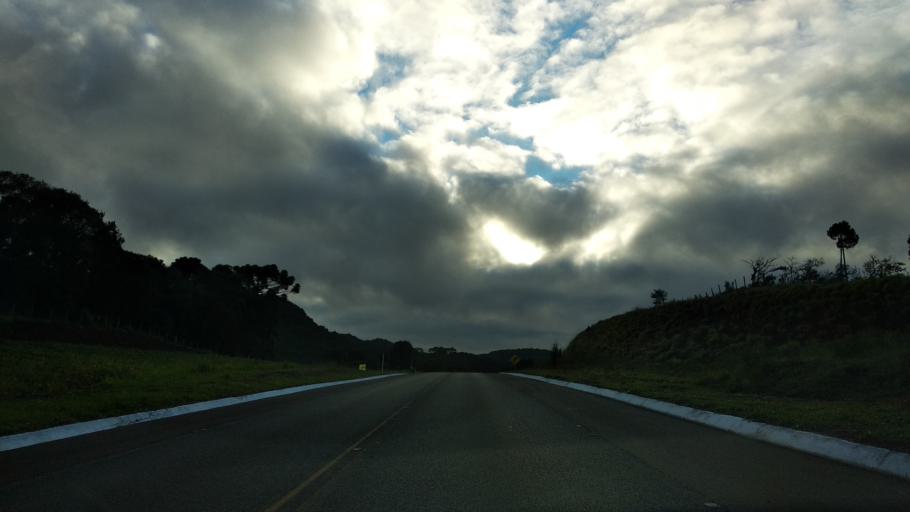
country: BR
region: Santa Catarina
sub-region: Curitibanos
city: Curitibanos
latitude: -27.5604
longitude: -50.8333
